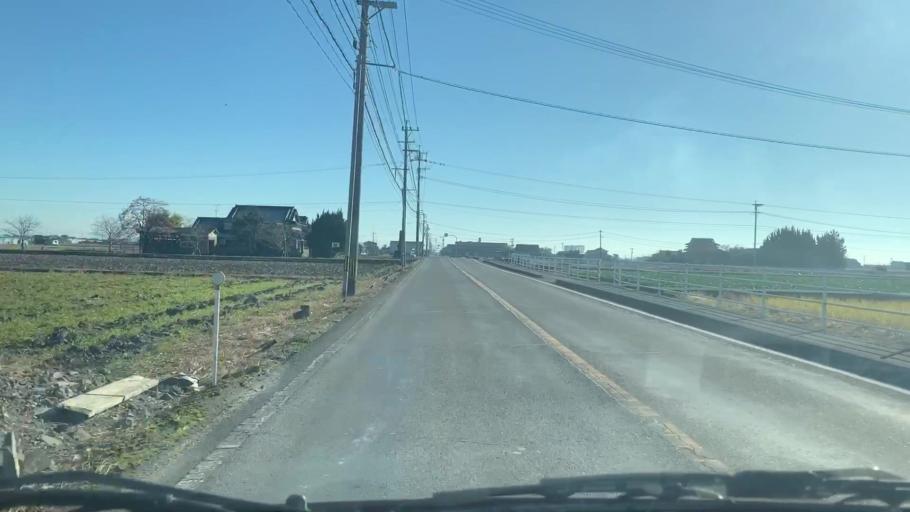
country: JP
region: Saga Prefecture
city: Kashima
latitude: 33.1847
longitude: 130.1594
